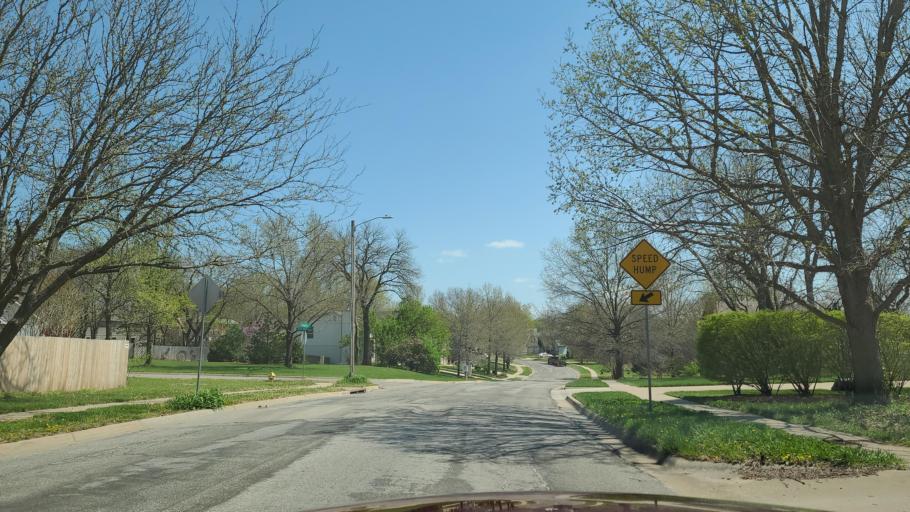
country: US
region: Kansas
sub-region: Douglas County
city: Lawrence
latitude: 38.9648
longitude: -95.2941
